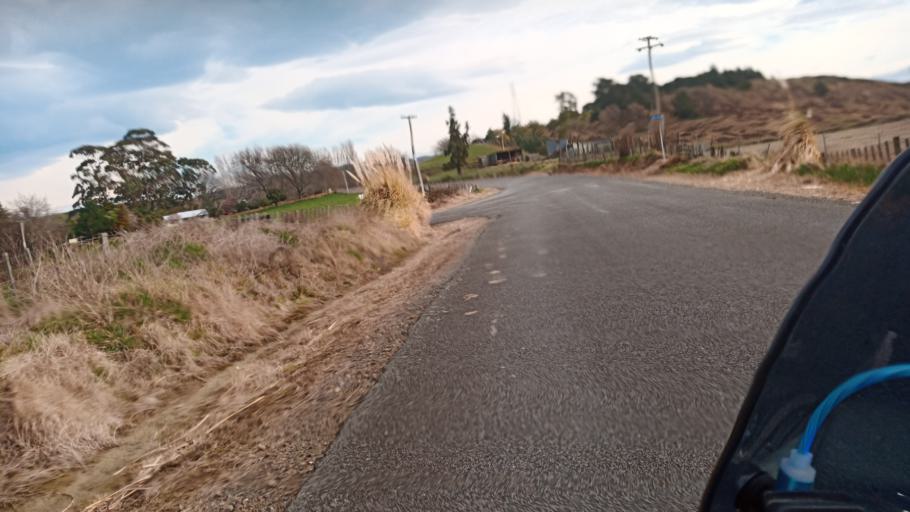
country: NZ
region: Hawke's Bay
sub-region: Wairoa District
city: Wairoa
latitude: -38.9730
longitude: 177.4338
